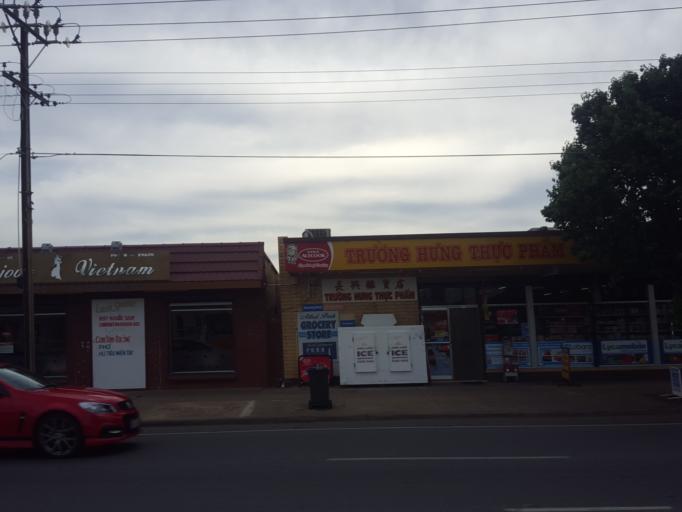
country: AU
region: South Australia
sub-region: Charles Sturt
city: Woodville North
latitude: -34.8581
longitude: 138.5472
